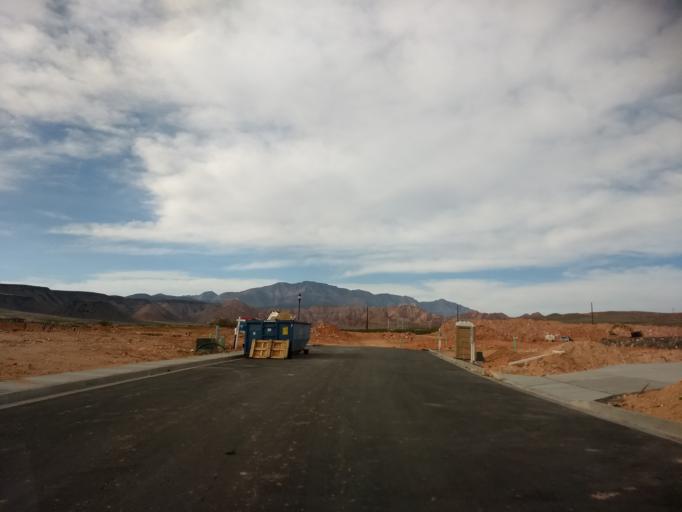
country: US
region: Utah
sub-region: Washington County
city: Washington
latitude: 37.1470
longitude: -113.5180
